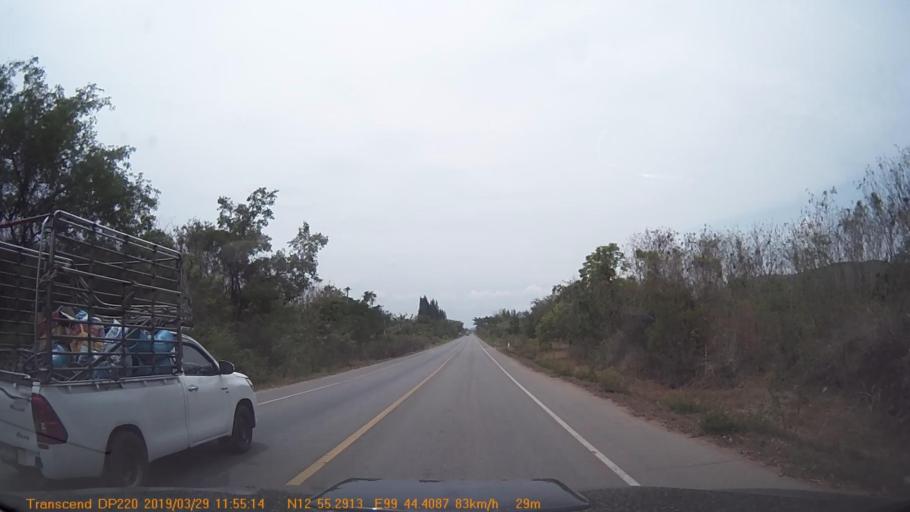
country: TH
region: Phetchaburi
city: Kaeng Krachan
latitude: 12.9213
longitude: 99.7399
